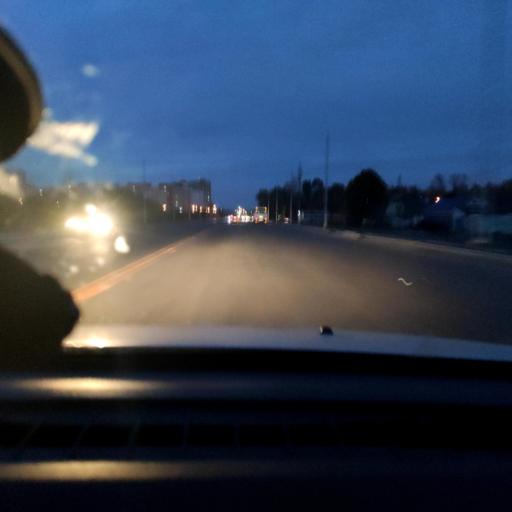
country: RU
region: Samara
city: Samara
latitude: 53.1137
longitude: 50.0836
